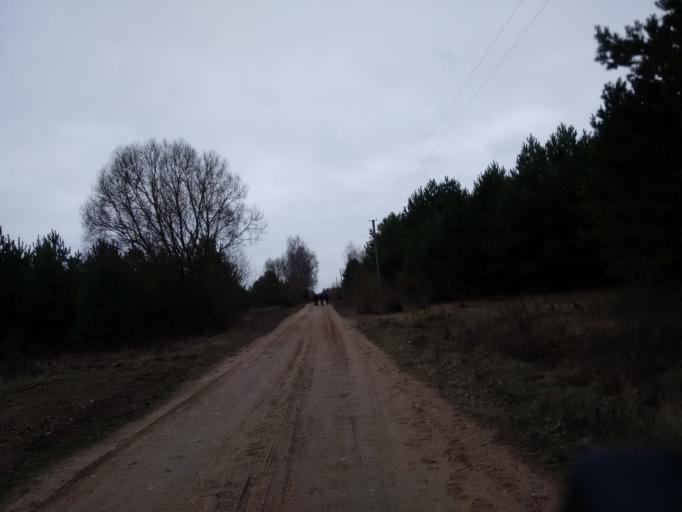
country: LT
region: Alytaus apskritis
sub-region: Alytus
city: Alytus
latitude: 54.2230
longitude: 23.9568
